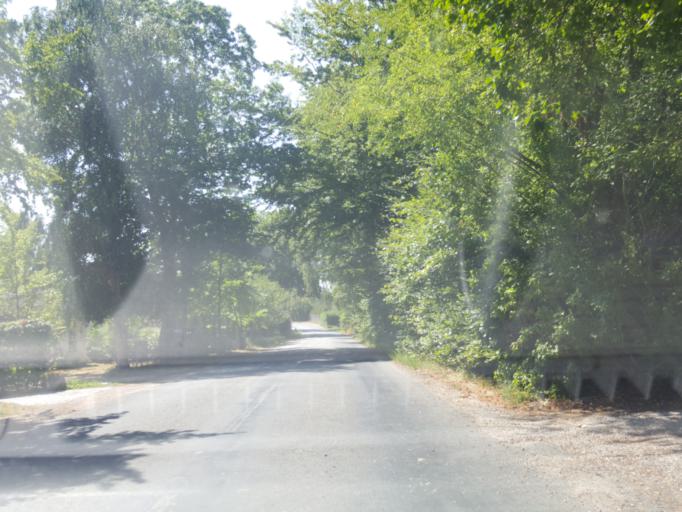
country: DK
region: Capital Region
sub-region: Fredensborg Kommune
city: Kokkedal
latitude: 55.9287
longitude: 12.4669
